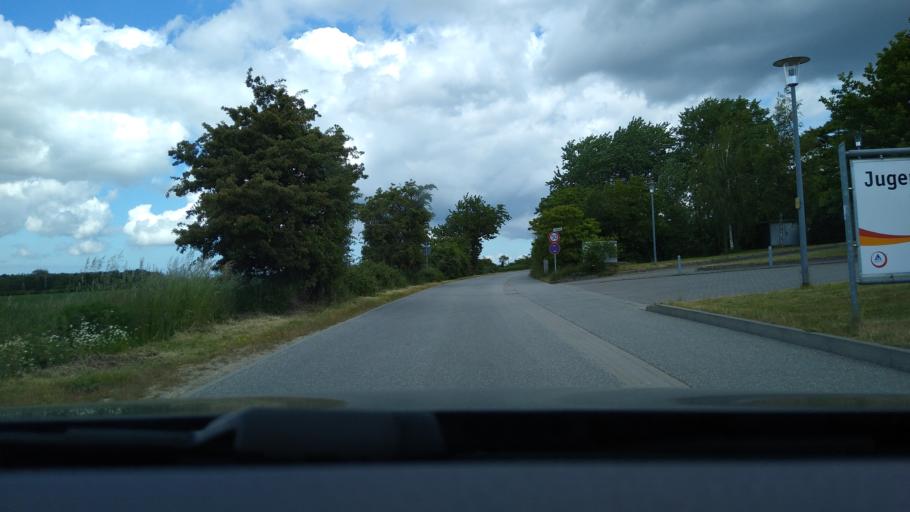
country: DE
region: Schleswig-Holstein
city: Dahme
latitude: 54.2072
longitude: 11.0897
